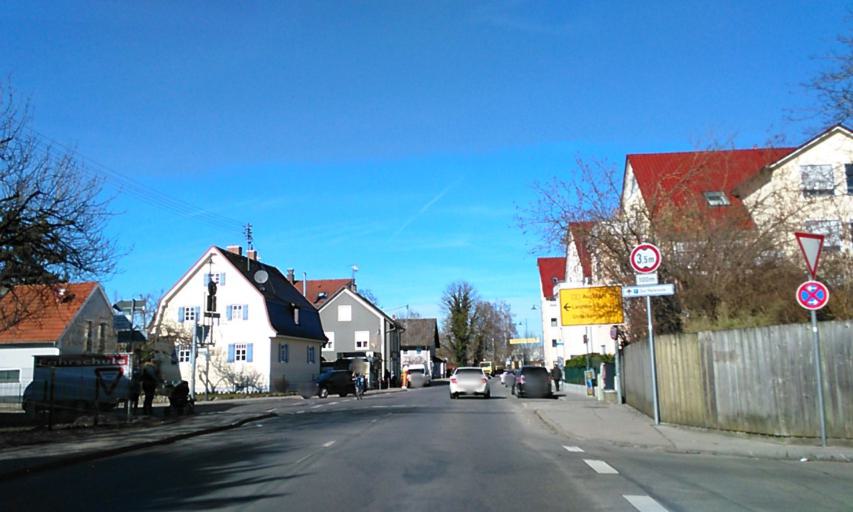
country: DE
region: Bavaria
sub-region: Swabia
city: Mering
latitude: 48.2625
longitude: 10.9848
